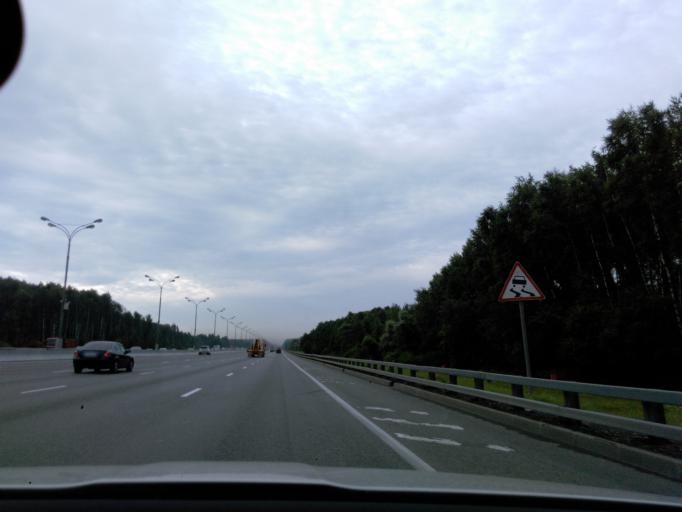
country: RU
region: Moskovskaya
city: Druzhba
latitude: 55.8747
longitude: 37.7405
